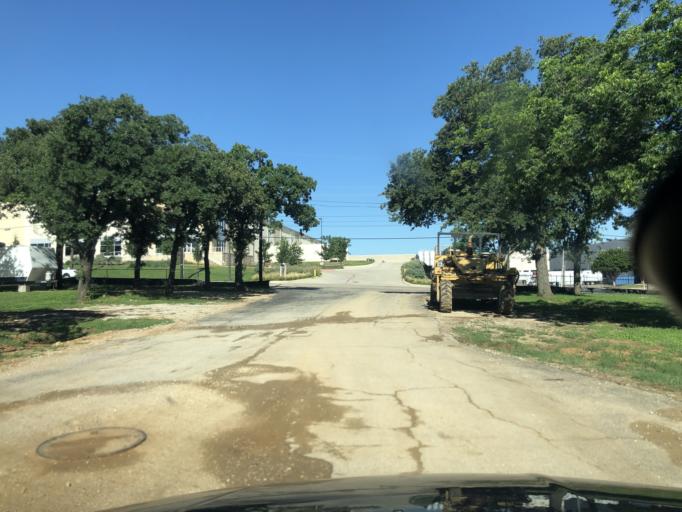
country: US
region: Texas
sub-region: Tarrant County
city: Euless
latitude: 32.8242
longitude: -97.0298
